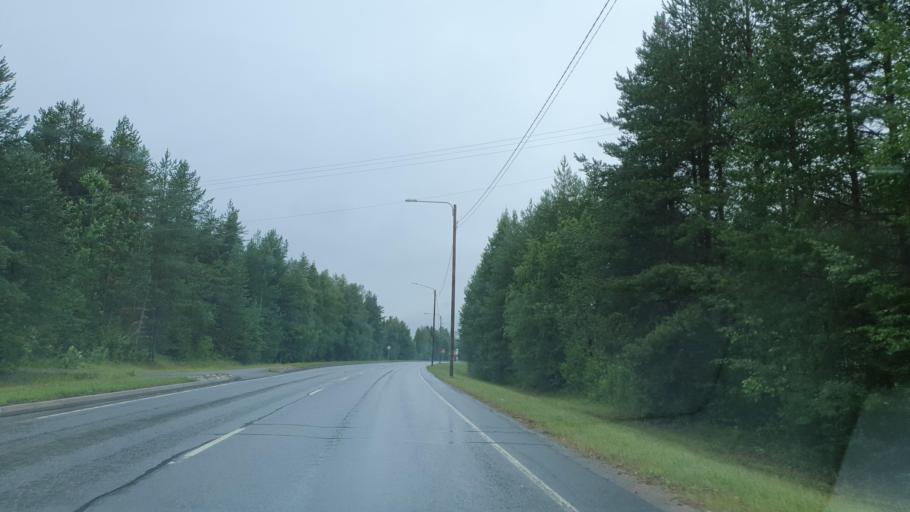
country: FI
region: Lapland
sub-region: Itae-Lappi
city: Kemijaervi
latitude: 66.7133
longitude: 27.4939
